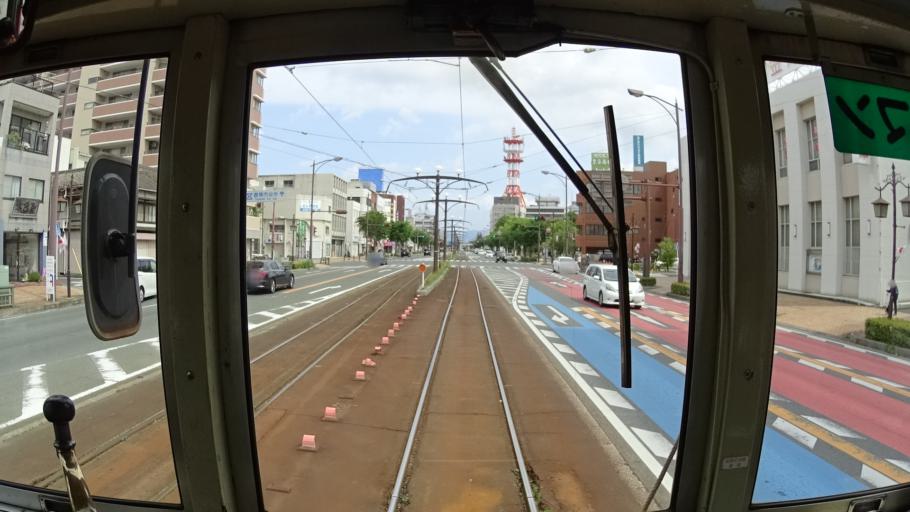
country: JP
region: Aichi
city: Toyohashi
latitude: 34.7633
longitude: 137.3902
